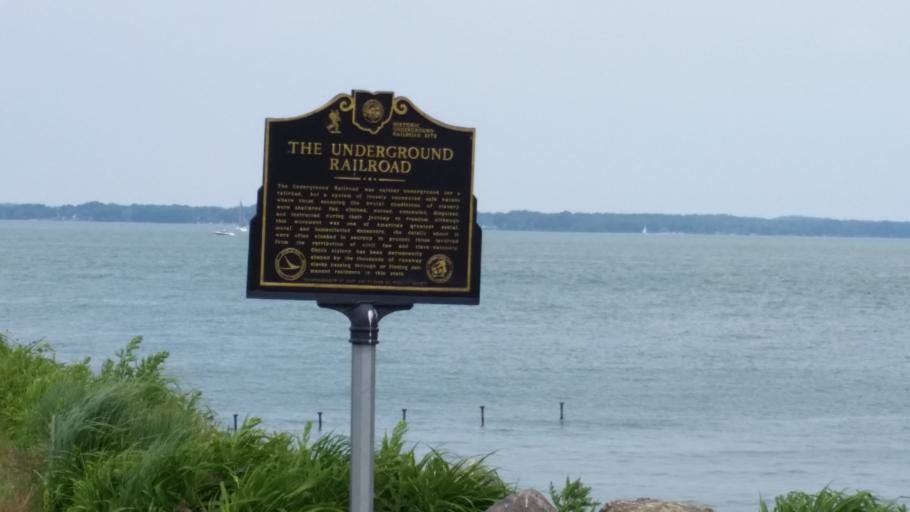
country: US
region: Ohio
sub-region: Erie County
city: Sandusky
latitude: 41.4593
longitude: -82.7080
